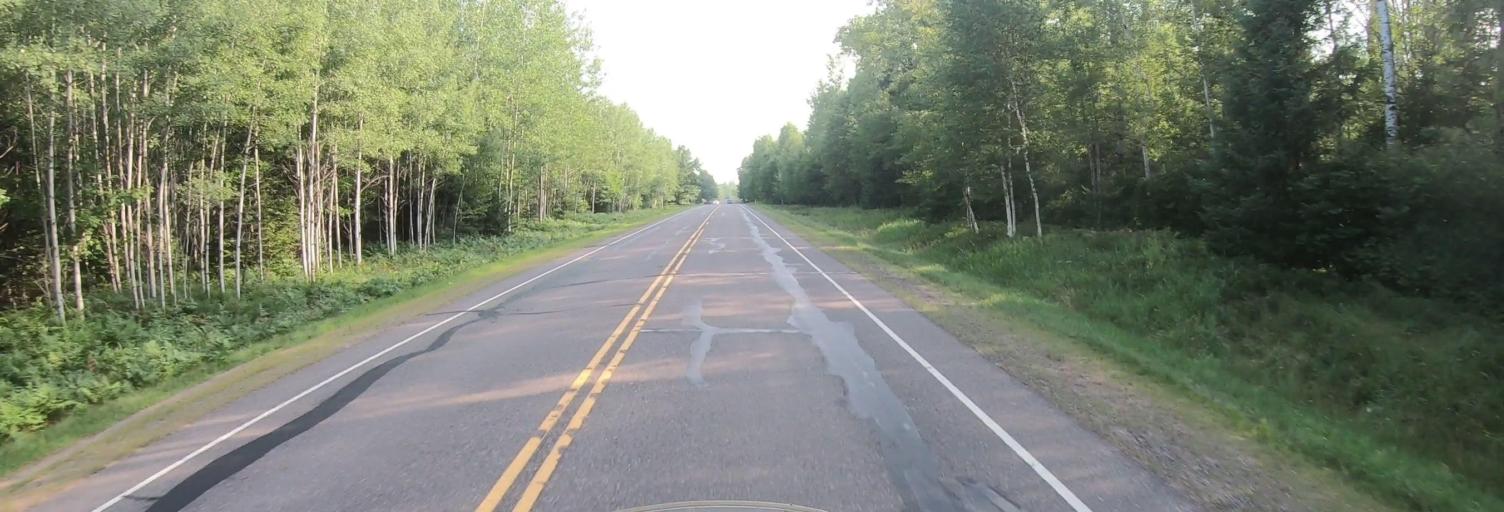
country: US
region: Wisconsin
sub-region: Ashland County
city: Ashland
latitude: 46.1610
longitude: -90.9138
